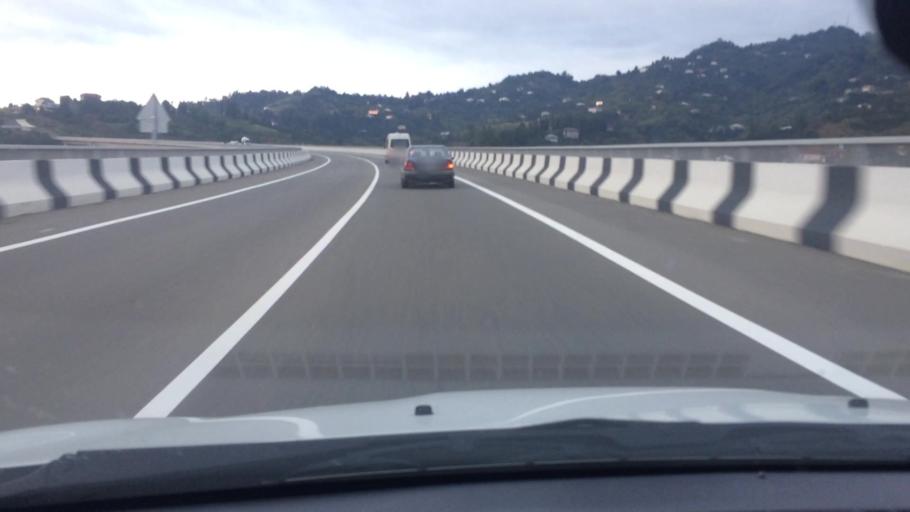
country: GE
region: Ajaria
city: Makhinjauri
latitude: 41.7131
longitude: 41.7521
